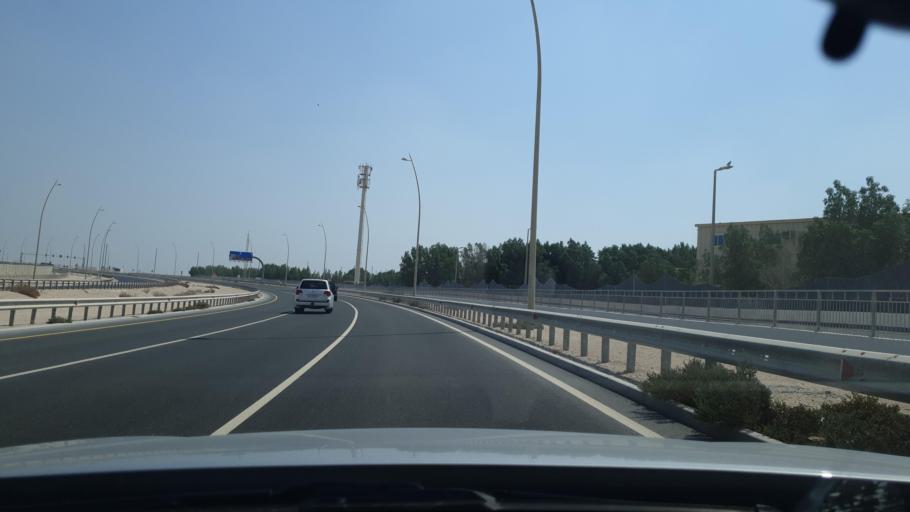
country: QA
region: Al Khawr
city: Al Khawr
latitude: 25.6608
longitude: 51.4804
